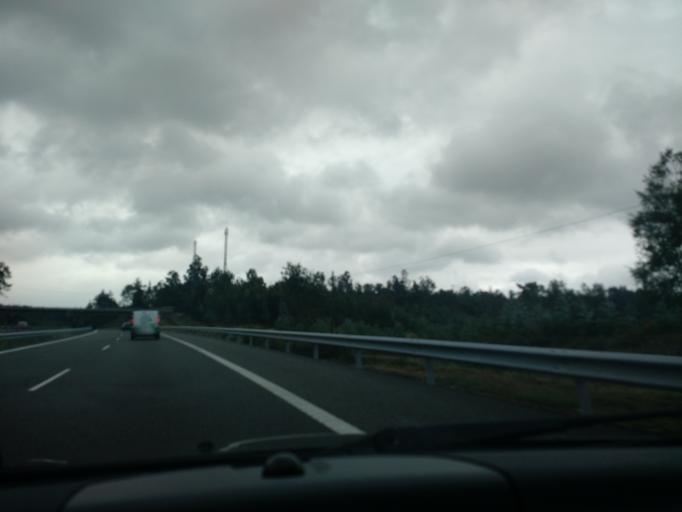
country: ES
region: Galicia
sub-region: Provincia da Coruna
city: Ordes
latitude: 43.0488
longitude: -8.3759
